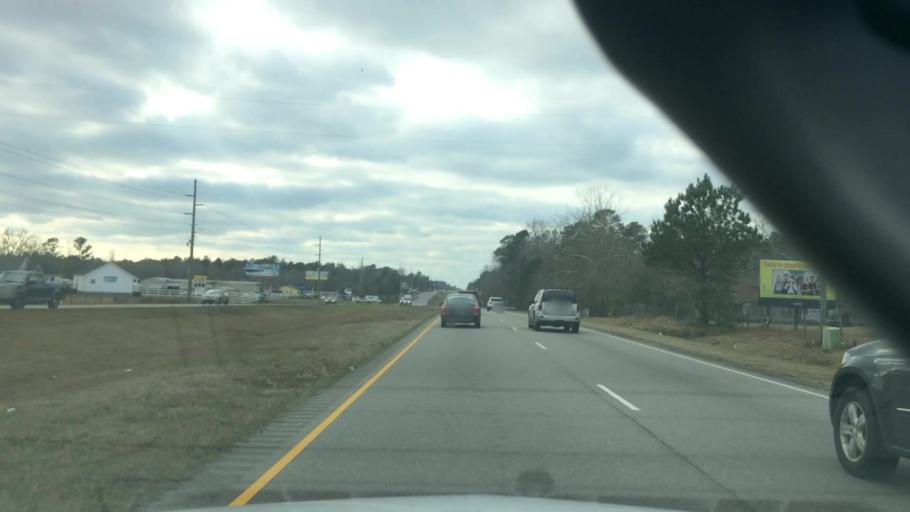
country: US
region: North Carolina
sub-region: Brunswick County
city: Shallotte
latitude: 34.0138
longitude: -78.2833
